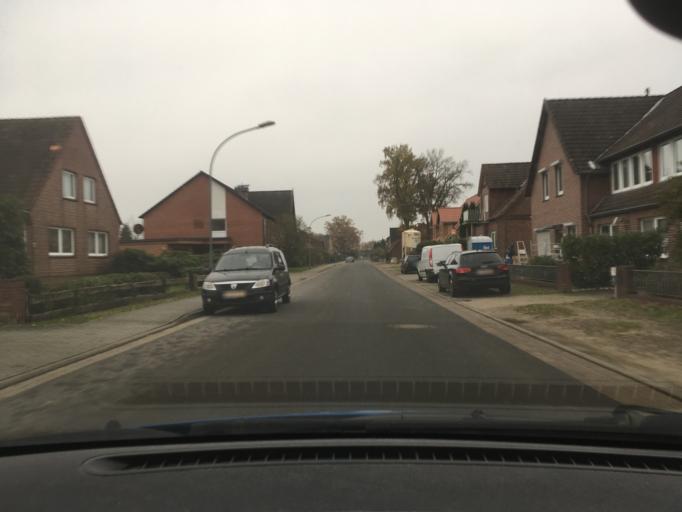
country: DE
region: Lower Saxony
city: Winsen
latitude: 53.3486
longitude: 10.2277
